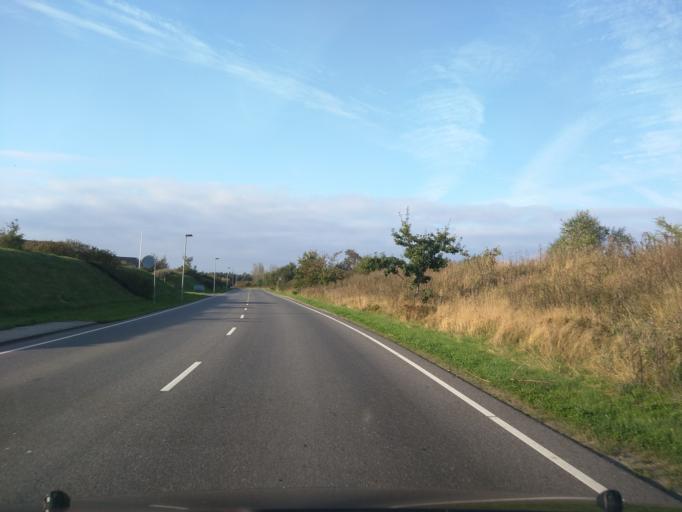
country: DK
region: Central Jutland
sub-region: Viborg Kommune
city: Viborg
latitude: 56.4685
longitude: 9.3801
